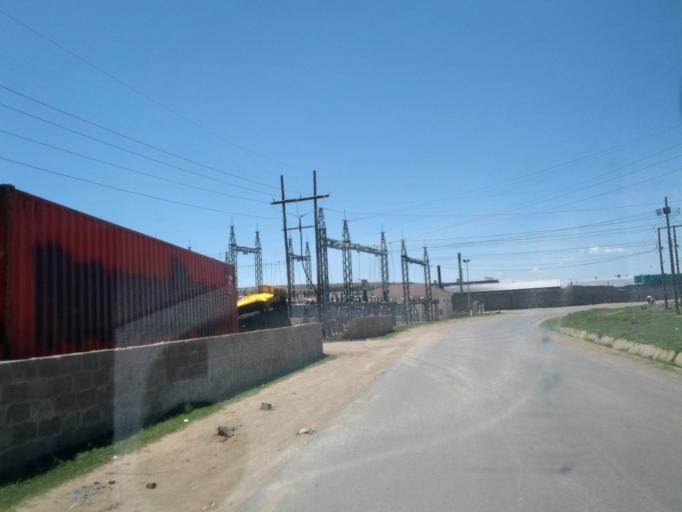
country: LS
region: Maseru
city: Maseru
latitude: -29.2966
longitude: 27.4642
